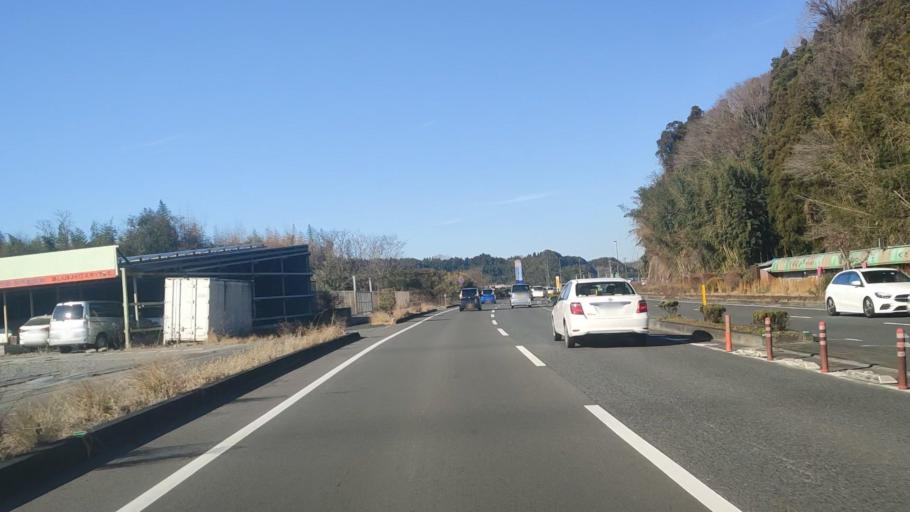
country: JP
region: Oita
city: Oita
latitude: 33.1152
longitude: 131.6543
